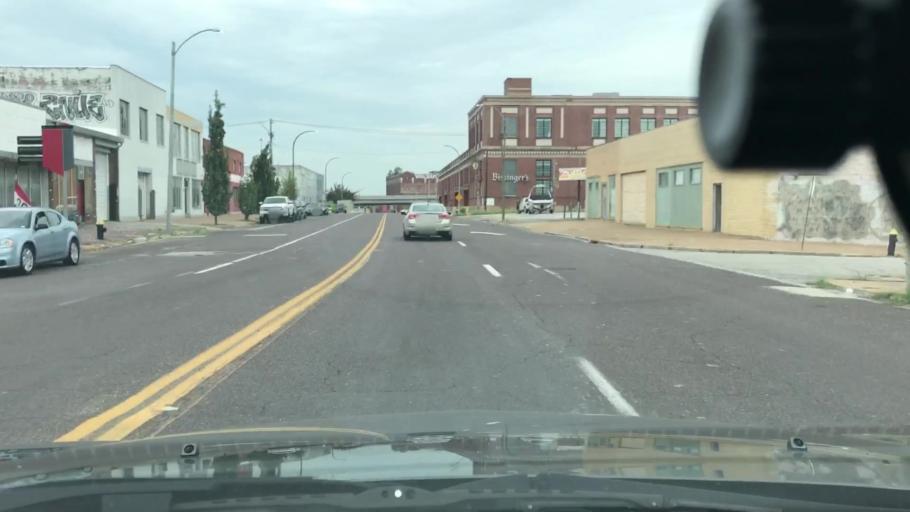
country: US
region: Missouri
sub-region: City of Saint Louis
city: St. Louis
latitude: 38.6400
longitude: -90.1859
